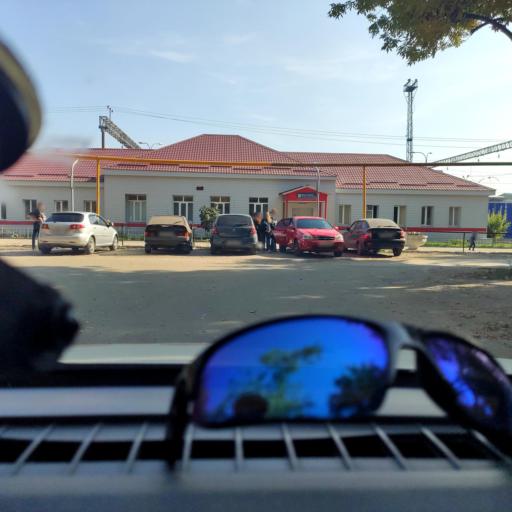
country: RU
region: Samara
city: Petra-Dubrava
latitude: 53.2337
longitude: 50.2872
